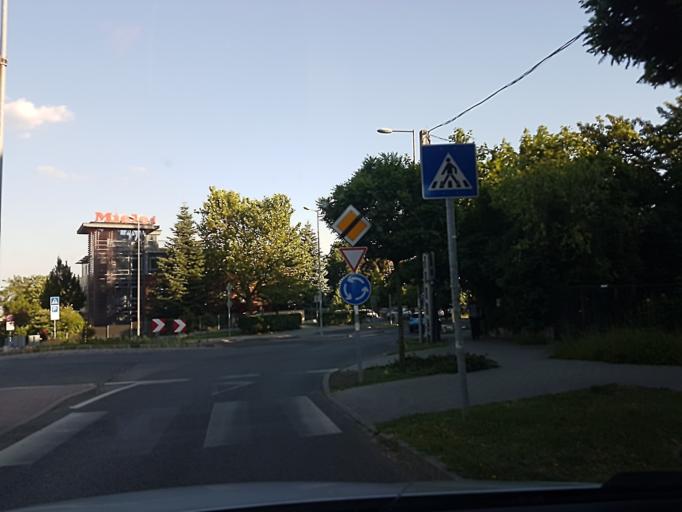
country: HU
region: Budapest
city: Budapest II. keruelet
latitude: 47.5200
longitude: 19.0219
